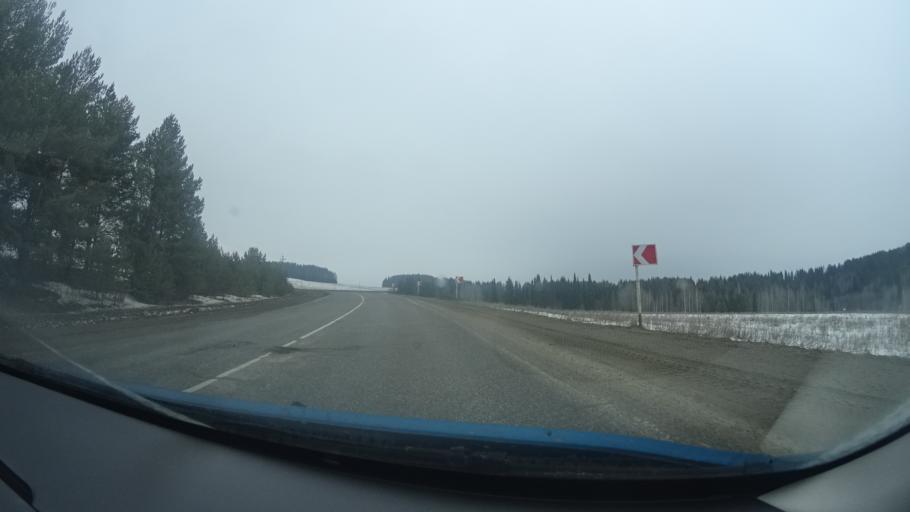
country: RU
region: Perm
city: Osa
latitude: 57.3070
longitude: 55.6202
